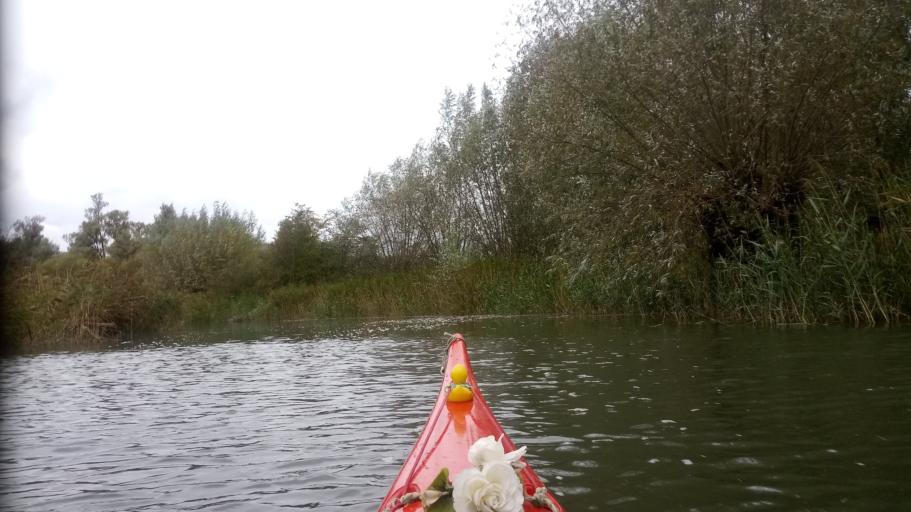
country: NL
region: North Brabant
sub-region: Gemeente Made en Drimmelen
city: Drimmelen
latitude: 51.7521
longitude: 4.7664
